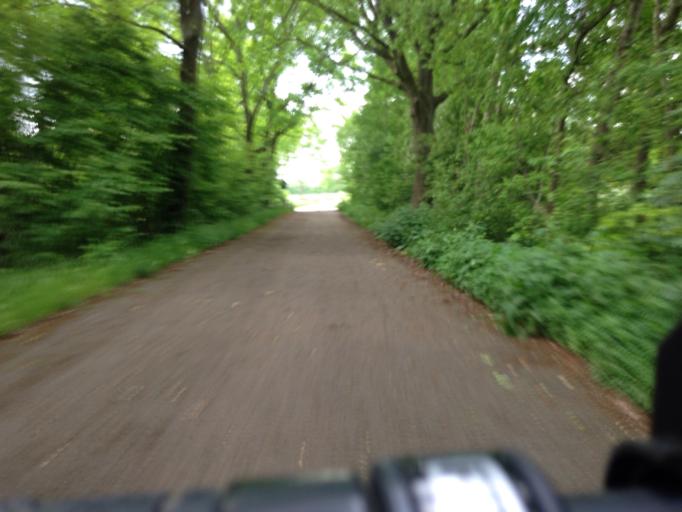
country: DE
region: Schleswig-Holstein
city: Barsbuettel
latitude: 53.5800
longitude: 10.1904
